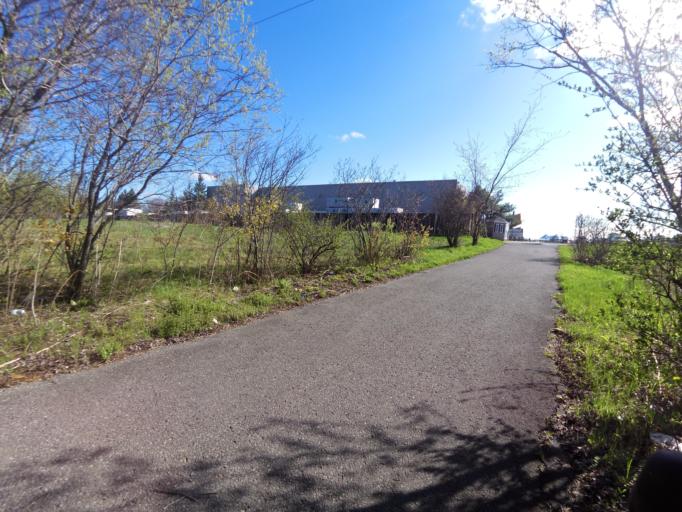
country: CA
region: Ontario
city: Ottawa
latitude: 45.3342
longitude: -75.7313
